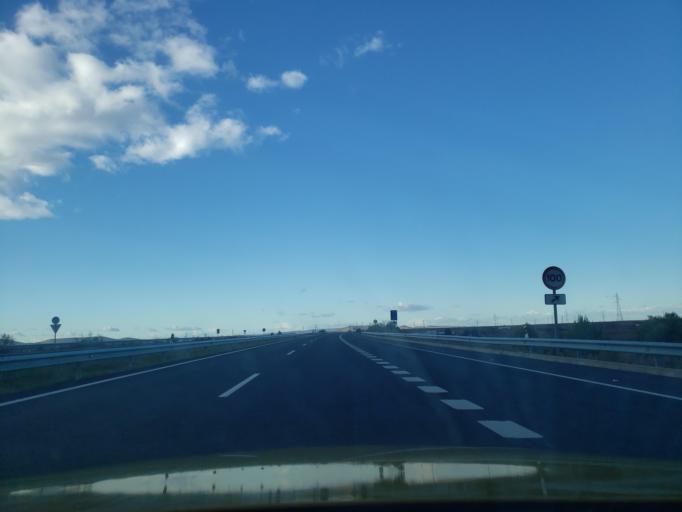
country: ES
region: Castille-La Mancha
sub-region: Province of Toledo
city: Madridejos
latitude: 39.4592
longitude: -3.5638
